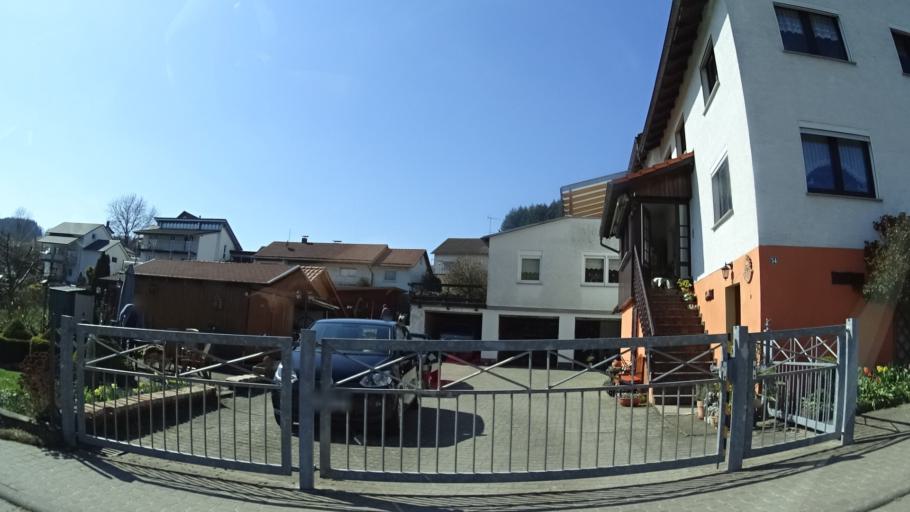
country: DE
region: Hesse
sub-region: Regierungsbezirk Darmstadt
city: Wald-Michelbach
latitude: 49.5878
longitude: 8.8145
